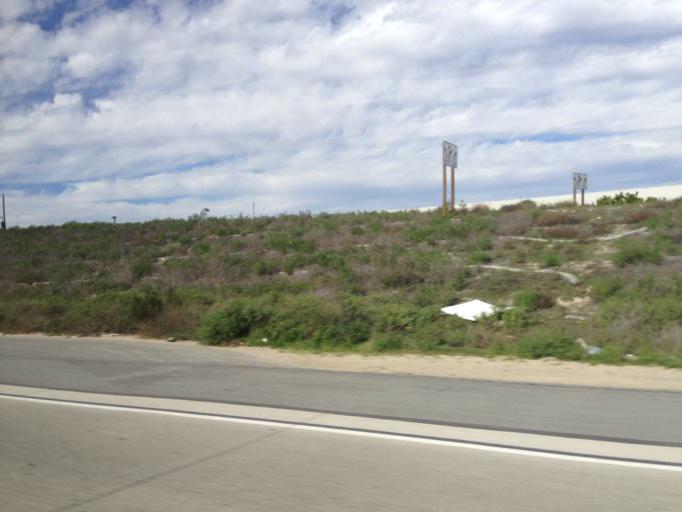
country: MX
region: Baja California
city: Tijuana
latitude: 32.5644
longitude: -116.9784
